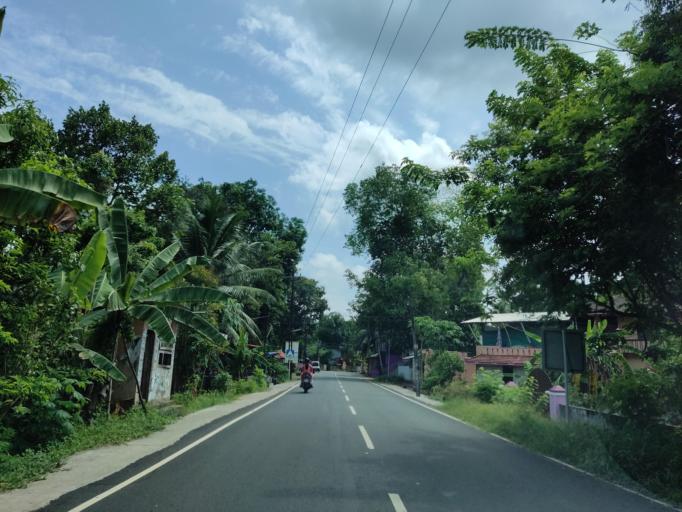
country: IN
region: Kerala
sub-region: Alappuzha
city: Mavelikara
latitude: 9.2681
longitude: 76.5652
